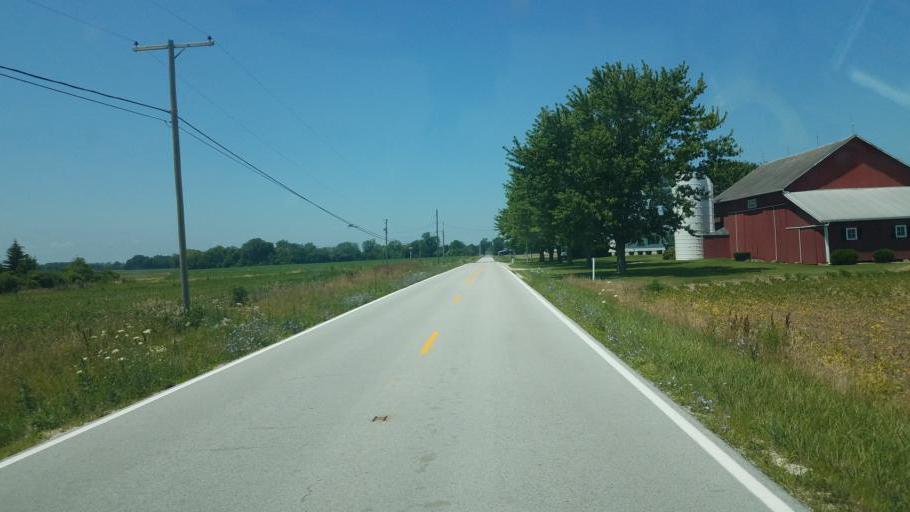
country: US
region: Ohio
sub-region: Sandusky County
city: Clyde
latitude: 41.3889
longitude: -83.0005
